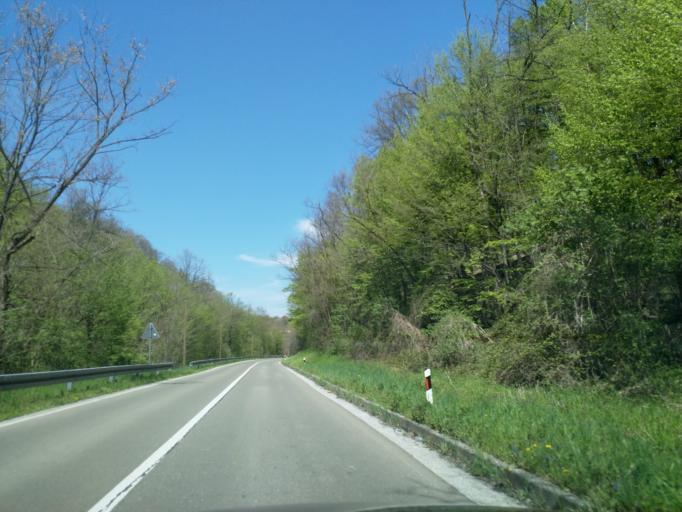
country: RS
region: Central Serbia
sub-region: Belgrade
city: Lazarevac
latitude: 44.3579
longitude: 20.3513
